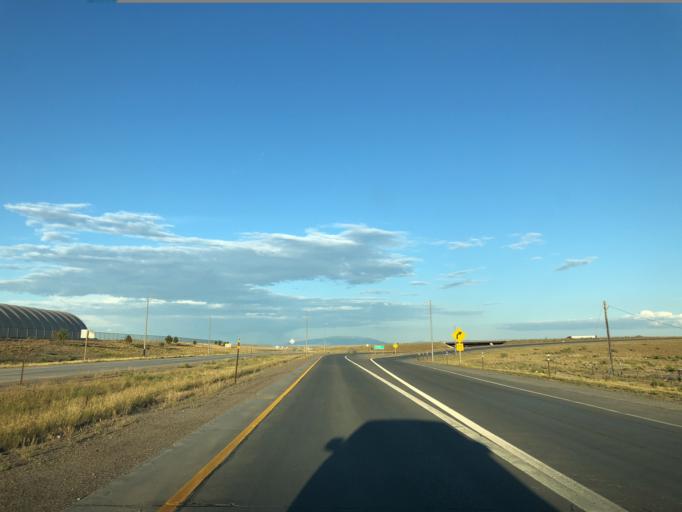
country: US
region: Wyoming
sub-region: Carbon County
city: Rawlins
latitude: 41.7913
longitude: -107.2053
